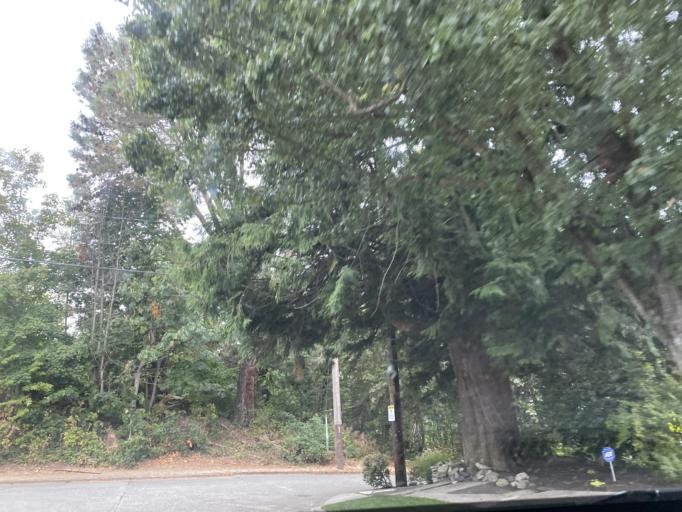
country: US
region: Washington
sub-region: King County
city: Seattle
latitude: 47.6450
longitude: -122.3578
